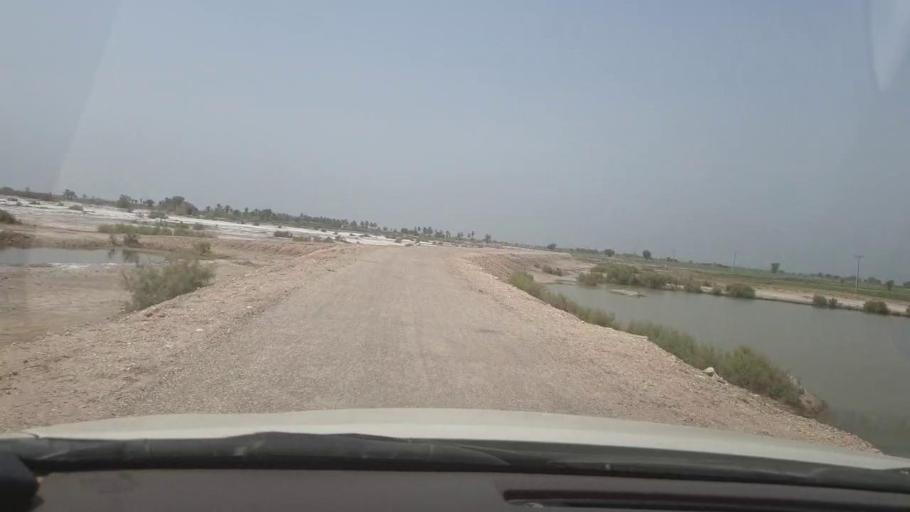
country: PK
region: Sindh
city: Garhi Yasin
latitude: 27.9736
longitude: 68.5484
